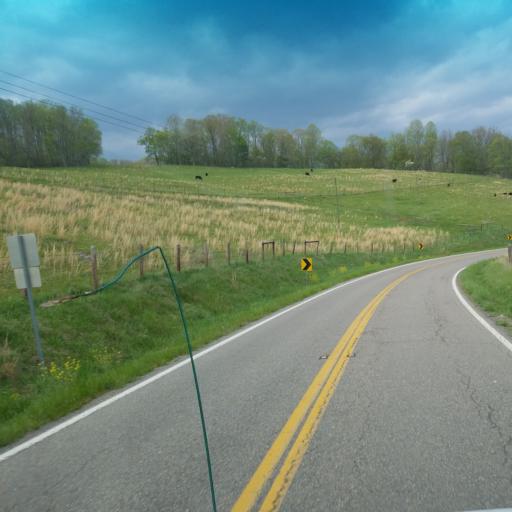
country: US
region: Virginia
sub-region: Smyth County
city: Marion
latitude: 36.9351
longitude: -81.5290
